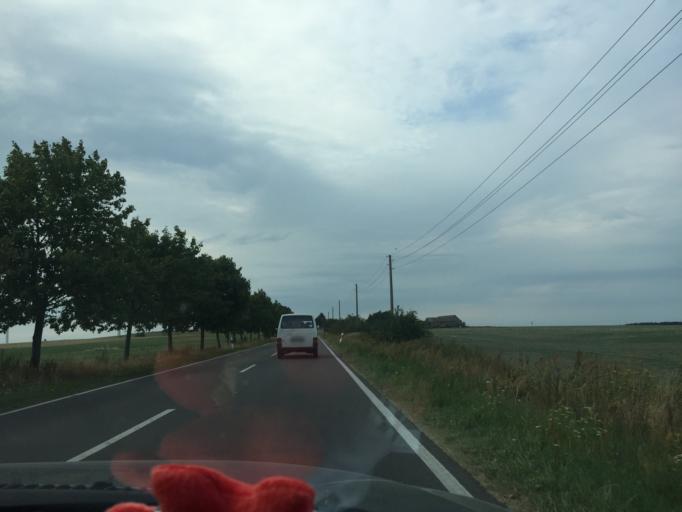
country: DE
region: Brandenburg
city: Zehdenick
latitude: 52.9896
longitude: 13.3060
